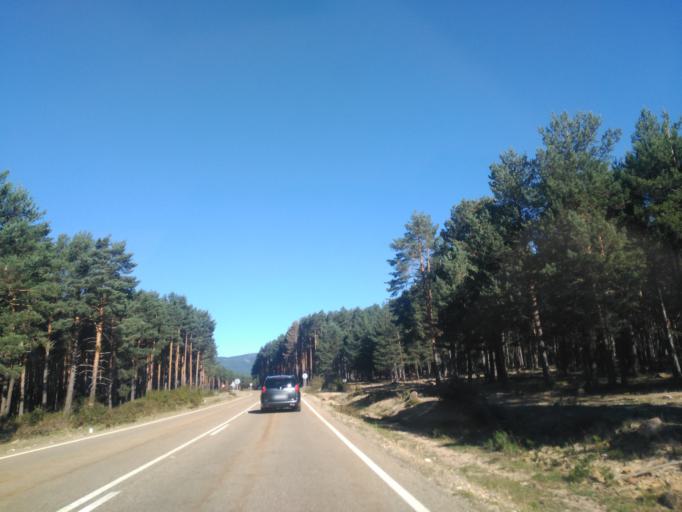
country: ES
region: Castille and Leon
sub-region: Provincia de Soria
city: Vinuesa
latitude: 41.9523
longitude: -2.7744
